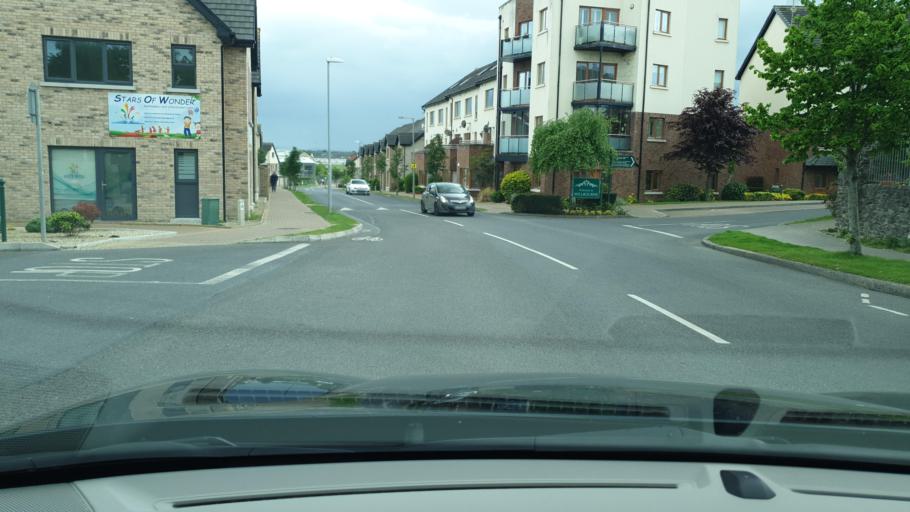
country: IE
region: Leinster
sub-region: An Mhi
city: Ashbourne
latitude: 53.5135
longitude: -6.4113
